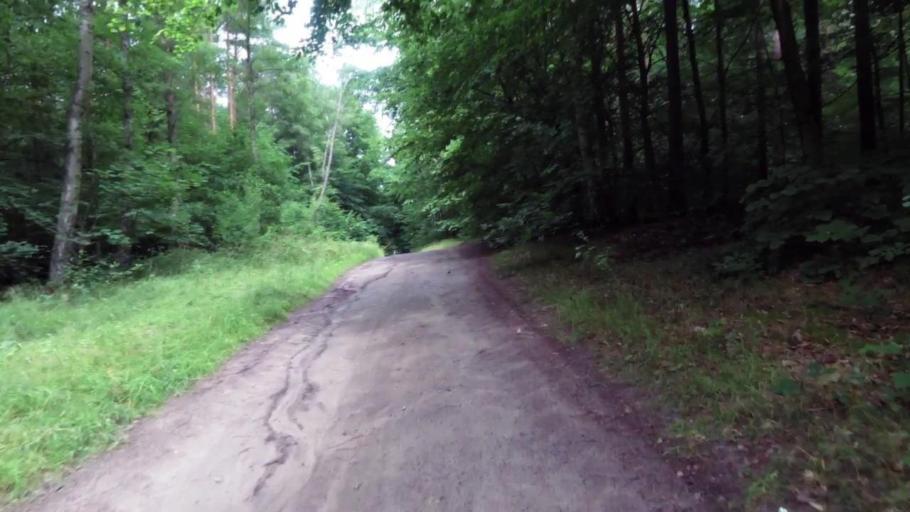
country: PL
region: West Pomeranian Voivodeship
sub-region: Powiat pyrzycki
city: Lipiany
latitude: 52.9775
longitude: 14.9249
